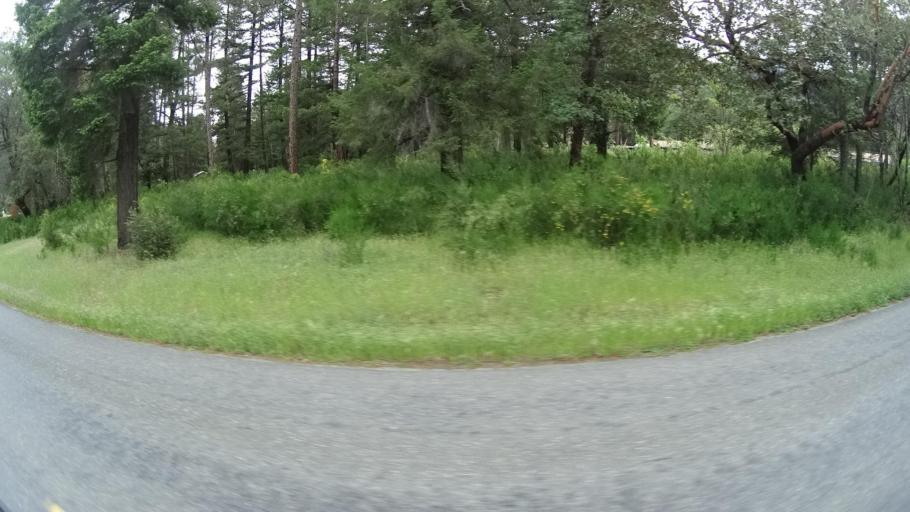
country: US
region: California
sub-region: Humboldt County
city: Willow Creek
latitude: 40.9479
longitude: -123.6303
